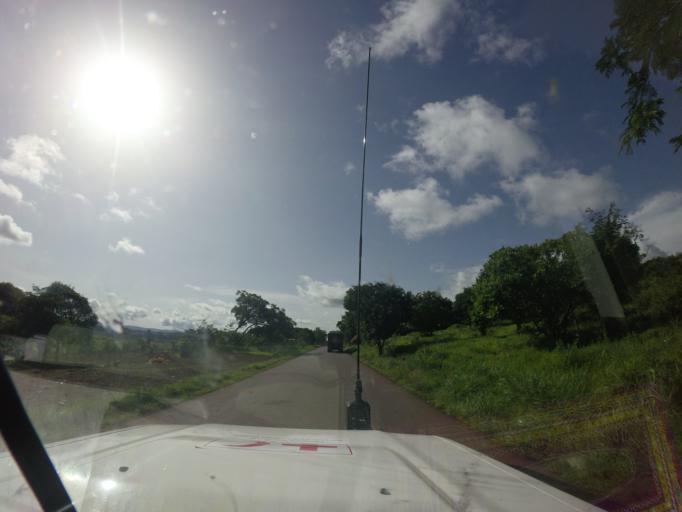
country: GN
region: Mamou
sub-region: Mamou Prefecture
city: Mamou
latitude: 10.2812
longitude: -12.4073
